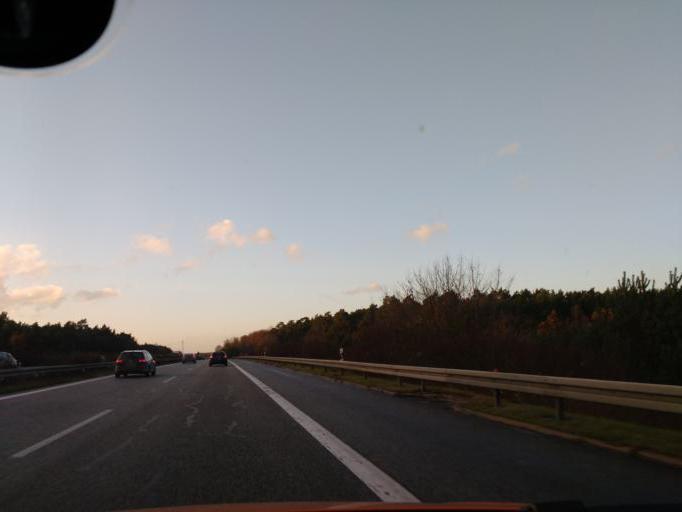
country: DE
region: Mecklenburg-Vorpommern
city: Sulstorf
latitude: 53.4780
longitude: 11.2957
